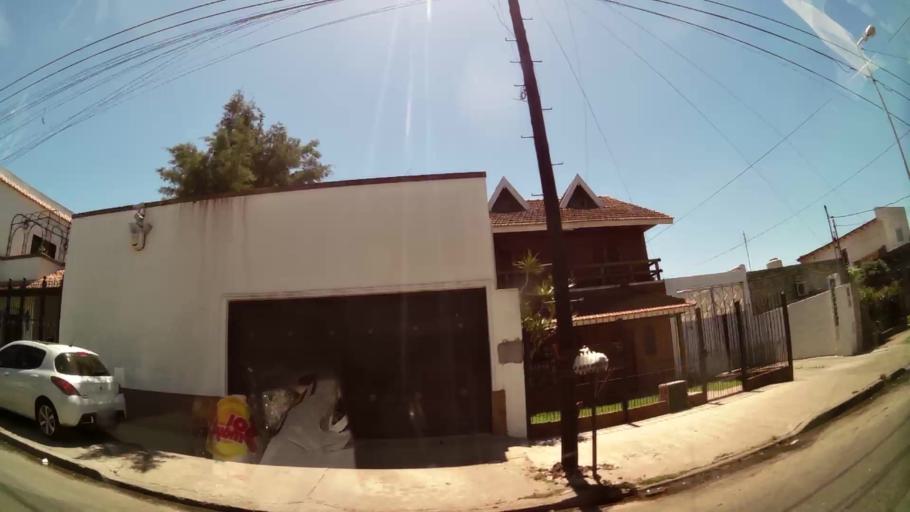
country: AR
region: Buenos Aires
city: Hurlingham
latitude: -34.4991
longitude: -58.6776
